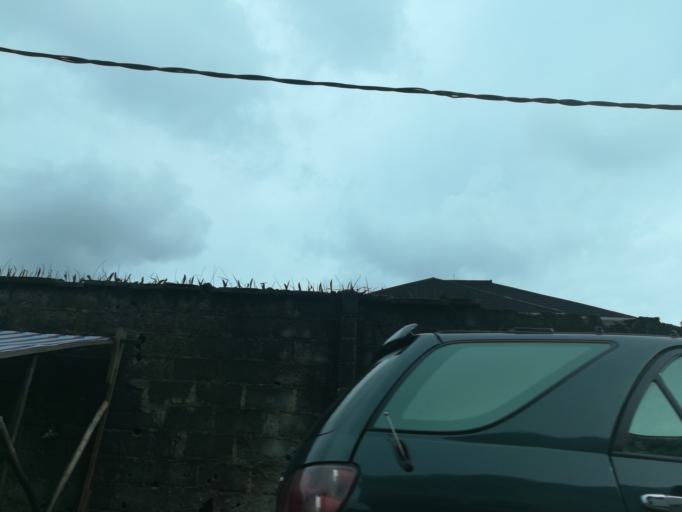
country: NG
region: Rivers
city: Port Harcourt
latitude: 4.8070
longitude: 6.9891
